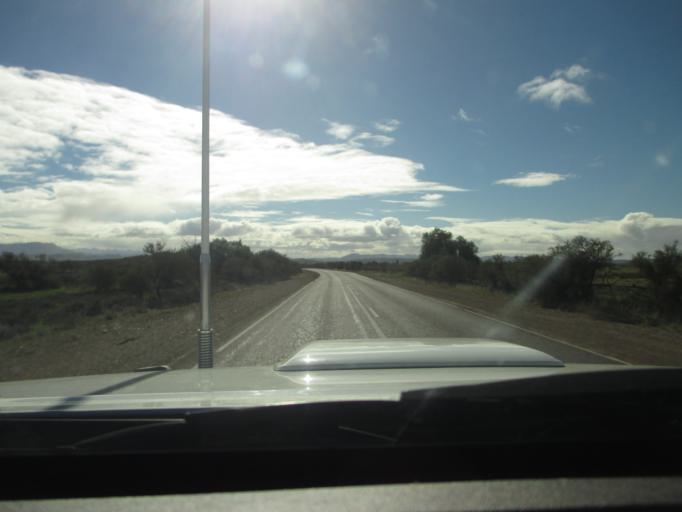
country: AU
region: South Australia
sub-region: Flinders Ranges
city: Quorn
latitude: -31.9106
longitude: 138.4324
